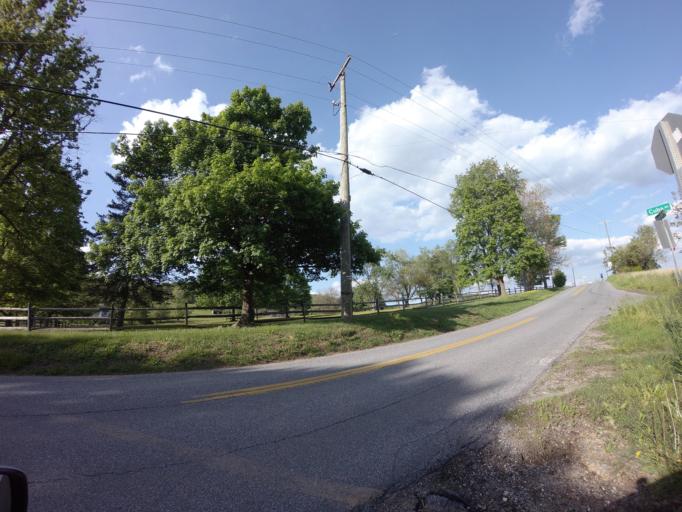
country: US
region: Maryland
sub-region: Baltimore County
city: Hunt Valley
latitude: 39.5320
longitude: -76.7175
